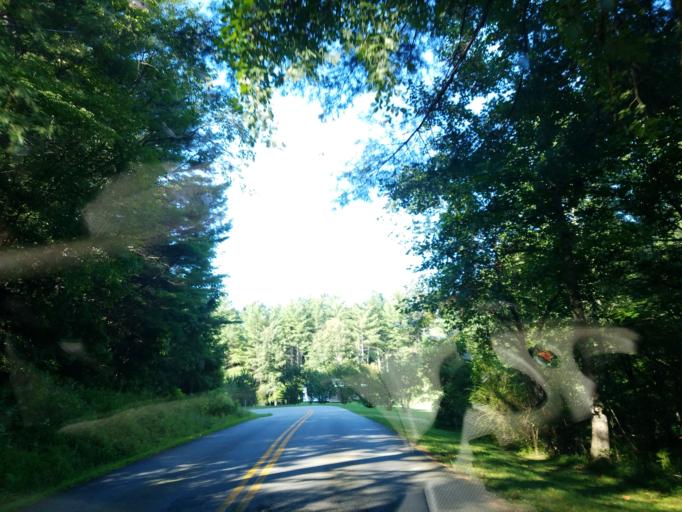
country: US
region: Georgia
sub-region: Union County
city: Blairsville
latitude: 34.7478
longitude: -84.1198
